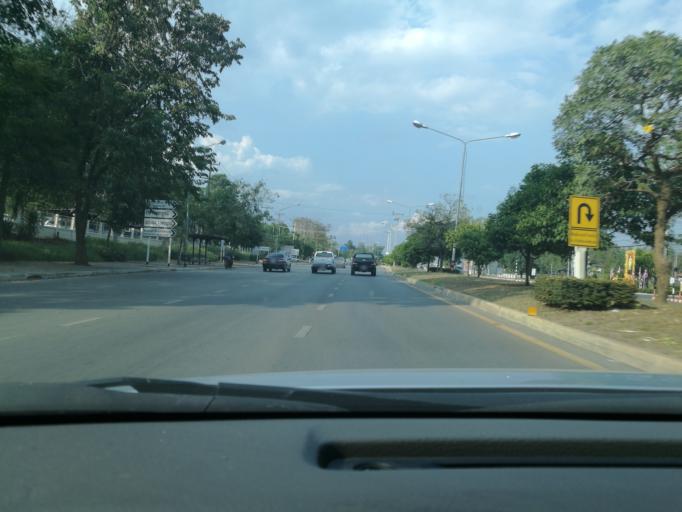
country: TH
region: Phetchabun
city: Phetchabun
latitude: 16.4394
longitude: 101.1516
